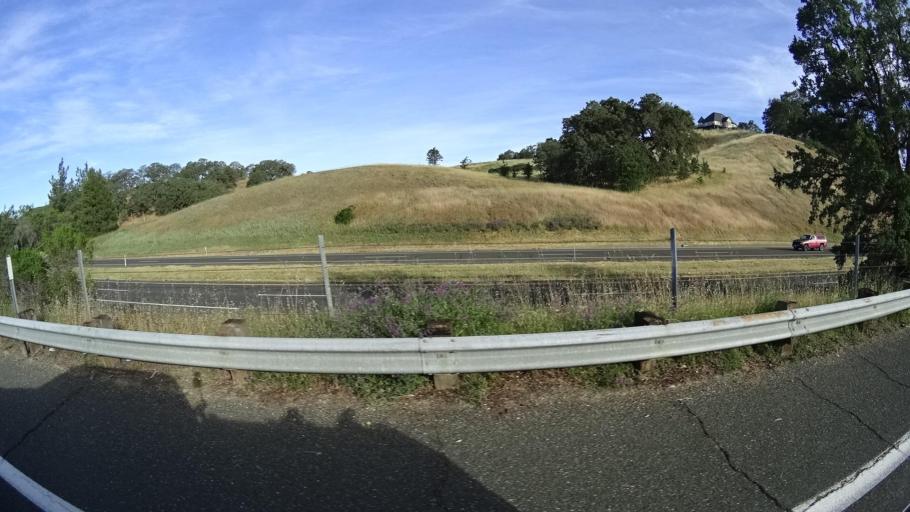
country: US
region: California
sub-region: Lake County
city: North Lakeport
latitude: 39.1141
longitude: -122.9063
